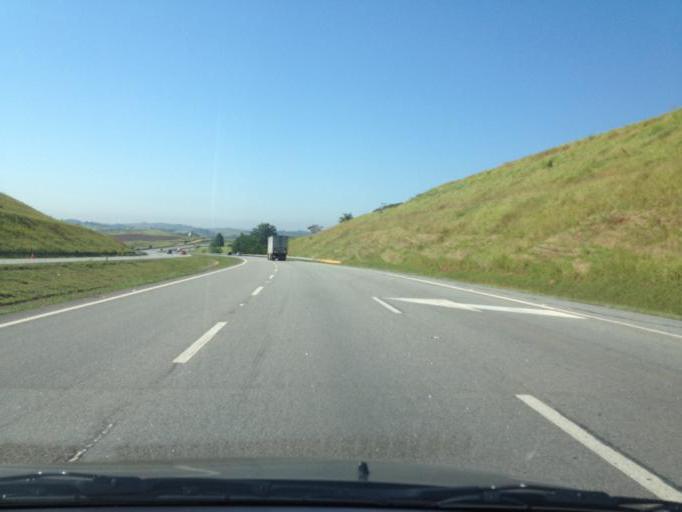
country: BR
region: Sao Paulo
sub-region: Guararema
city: Guararema
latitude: -23.3598
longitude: -46.0987
